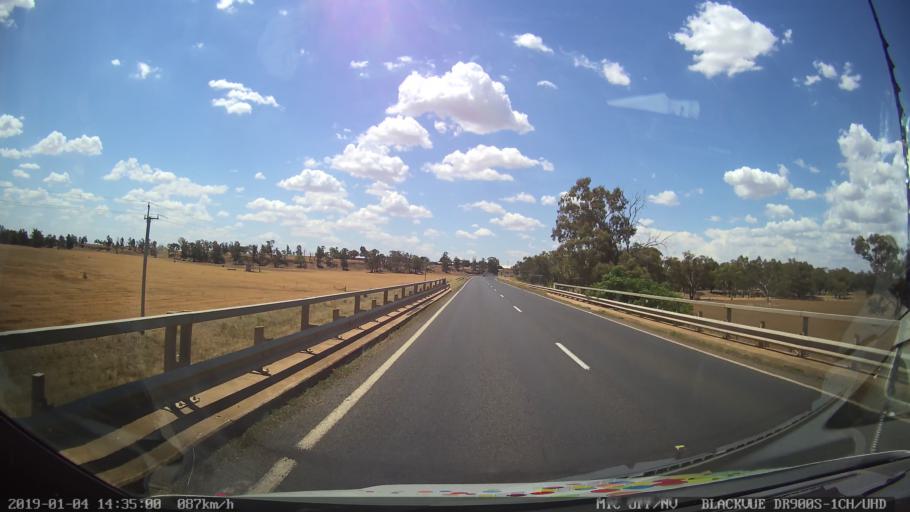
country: AU
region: New South Wales
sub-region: Dubbo Municipality
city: Dubbo
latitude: -32.1913
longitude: 148.6212
